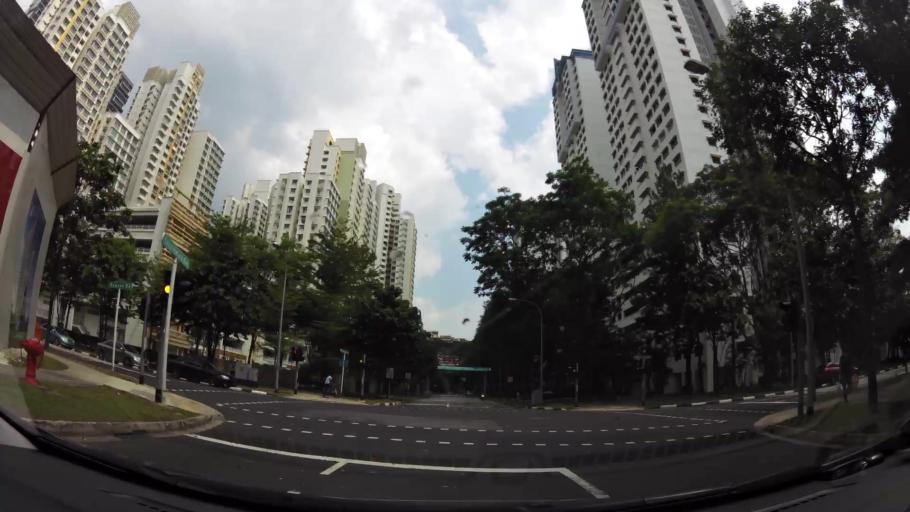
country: SG
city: Singapore
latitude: 1.2937
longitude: 103.8102
